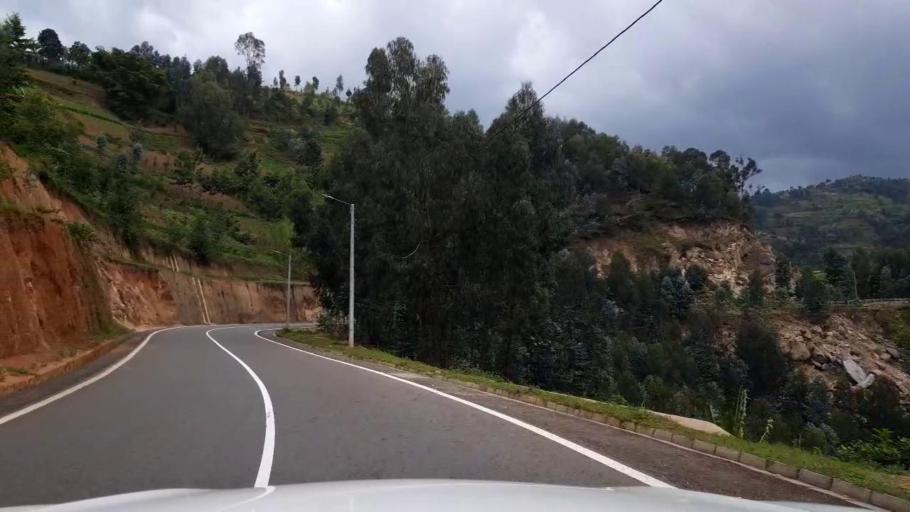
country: RW
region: Western Province
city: Kibuye
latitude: -1.9317
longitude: 29.3746
